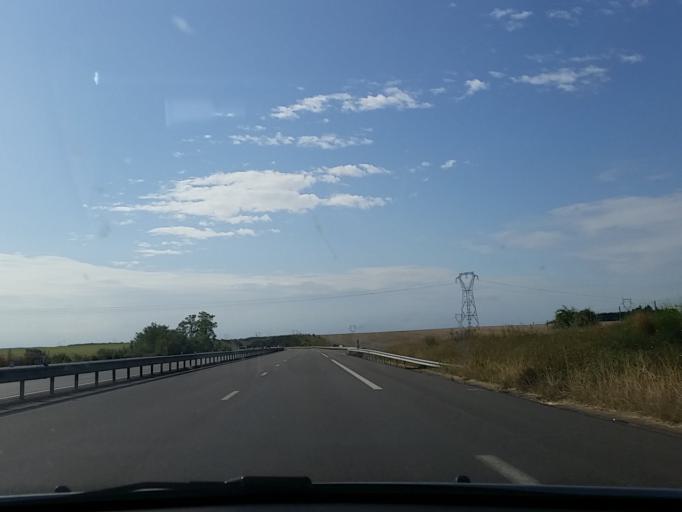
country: FR
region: Centre
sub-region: Departement du Cher
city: Trouy
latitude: 47.0196
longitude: 2.3813
